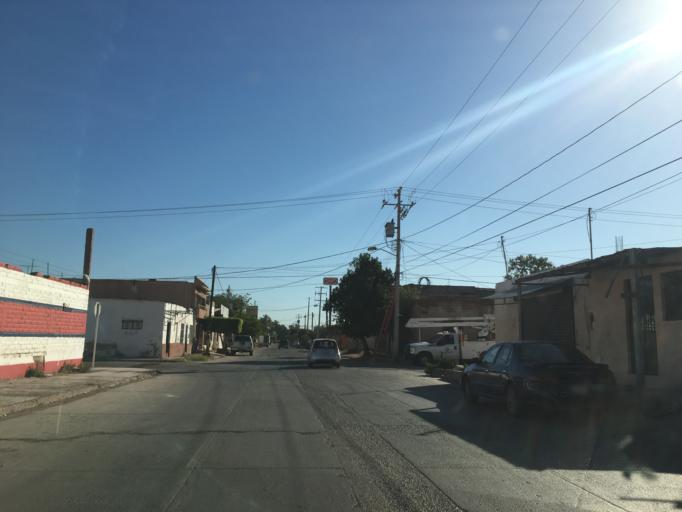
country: MX
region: Sonora
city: Heroica Guaymas
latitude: 27.9175
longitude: -110.8990
